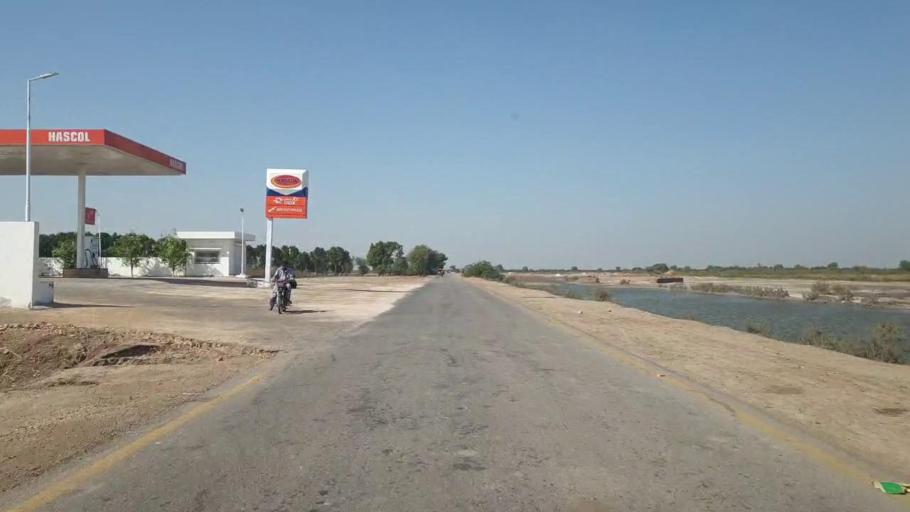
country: PK
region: Sindh
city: Rajo Khanani
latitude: 25.0068
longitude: 68.8362
